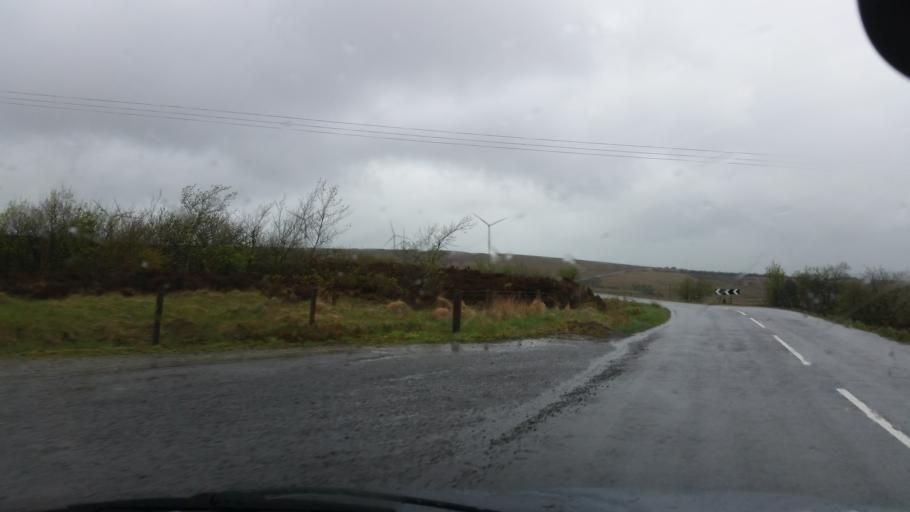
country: GB
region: Northern Ireland
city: Fivemiletown
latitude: 54.4375
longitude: -7.3261
